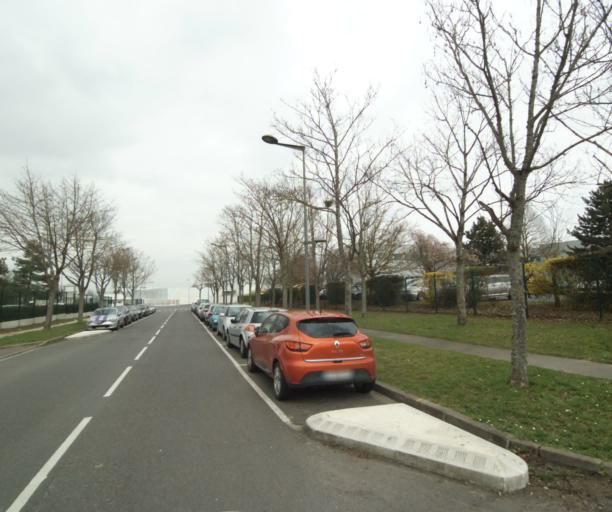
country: FR
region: Ile-de-France
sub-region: Departement du Val-d'Oise
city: Vaureal
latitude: 49.0541
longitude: 2.0402
